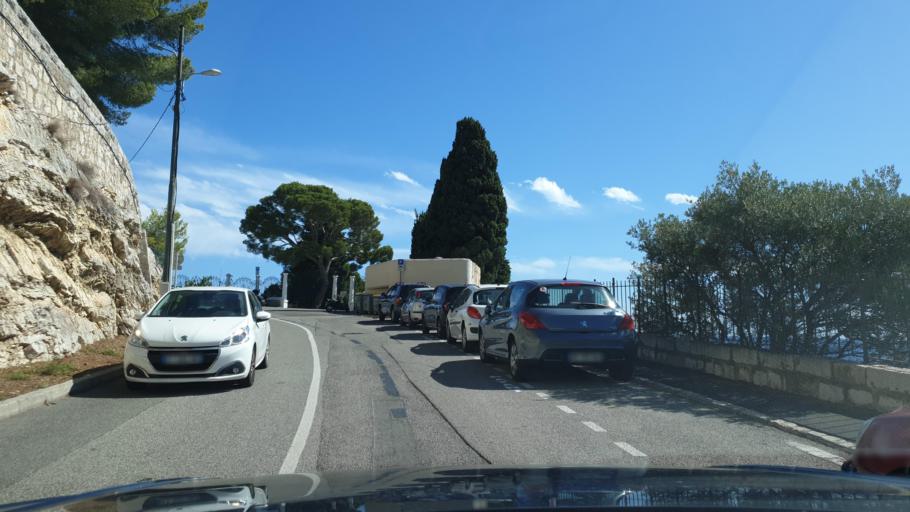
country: FR
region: Provence-Alpes-Cote d'Azur
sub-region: Departement des Alpes-Maritimes
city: Eze
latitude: 43.7188
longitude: 7.3723
